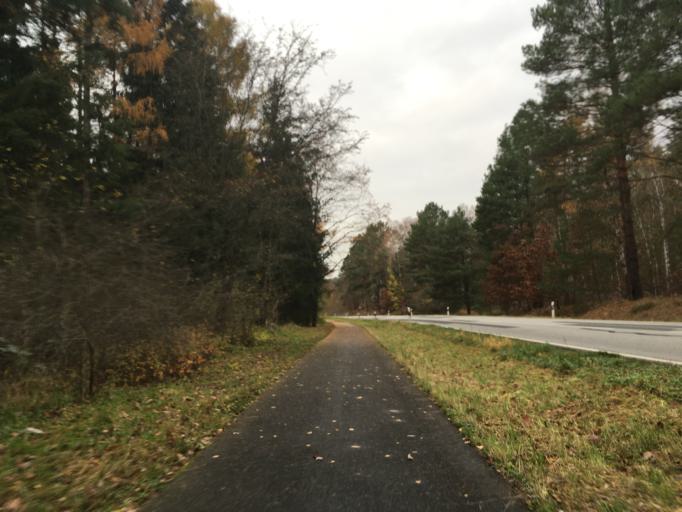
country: DE
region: Brandenburg
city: Mullrose
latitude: 52.2205
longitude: 14.4451
